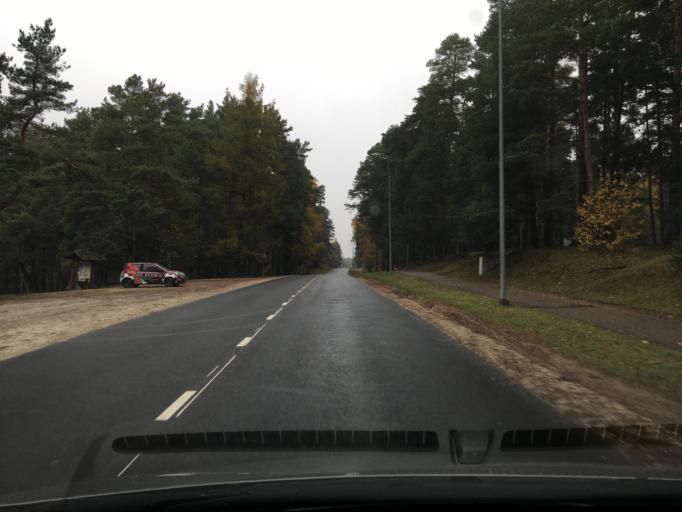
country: EE
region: Tartu
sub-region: Elva linn
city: Elva
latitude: 58.2252
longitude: 26.4071
